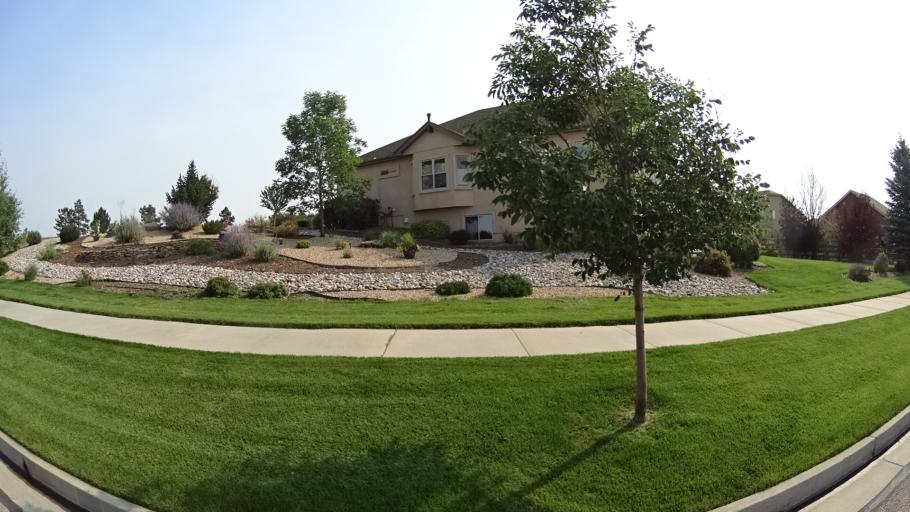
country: US
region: Colorado
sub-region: El Paso County
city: Black Forest
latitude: 38.9589
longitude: -104.7214
